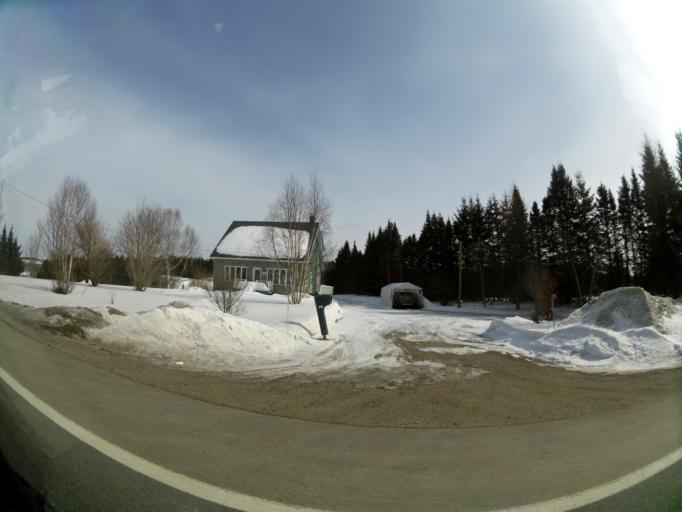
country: CA
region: Quebec
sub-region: Laurentides
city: Ferme-Neuve
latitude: 46.6424
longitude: -75.4788
